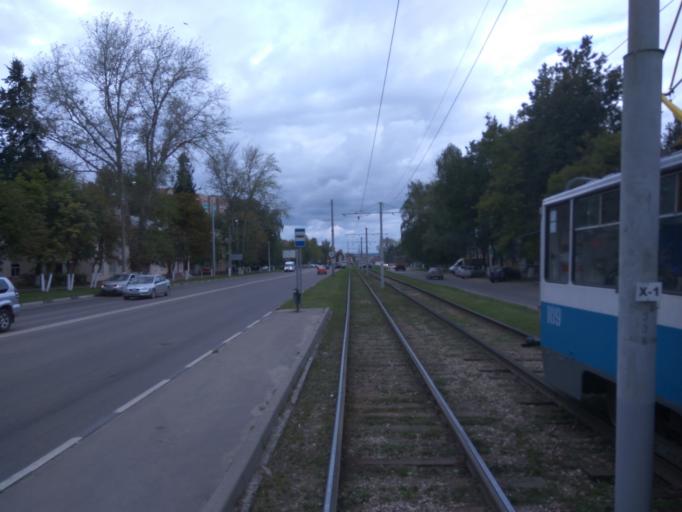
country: RU
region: Moskovskaya
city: Kolomna
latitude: 55.0811
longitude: 38.7627
